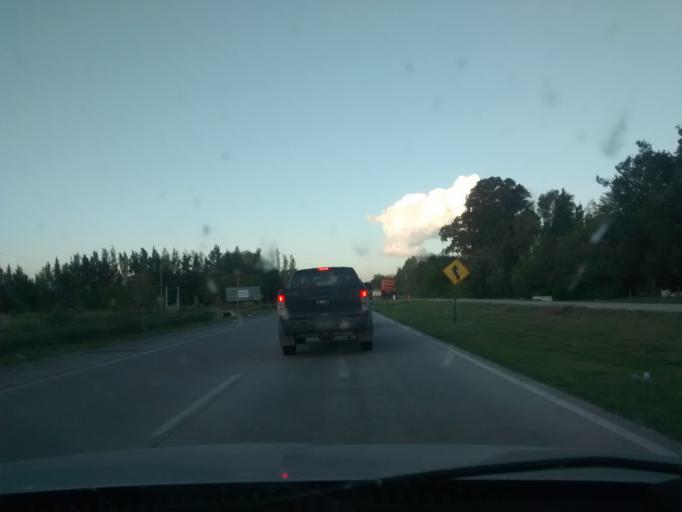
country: AR
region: Buenos Aires
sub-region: Partido de Brandsen
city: Brandsen
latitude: -35.0857
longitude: -58.1496
